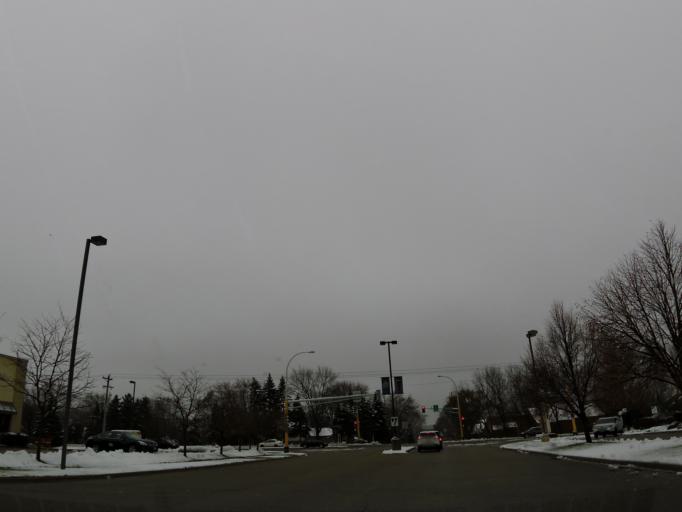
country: US
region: Minnesota
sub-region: Scott County
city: Prior Lake
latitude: 44.7471
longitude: -93.3846
